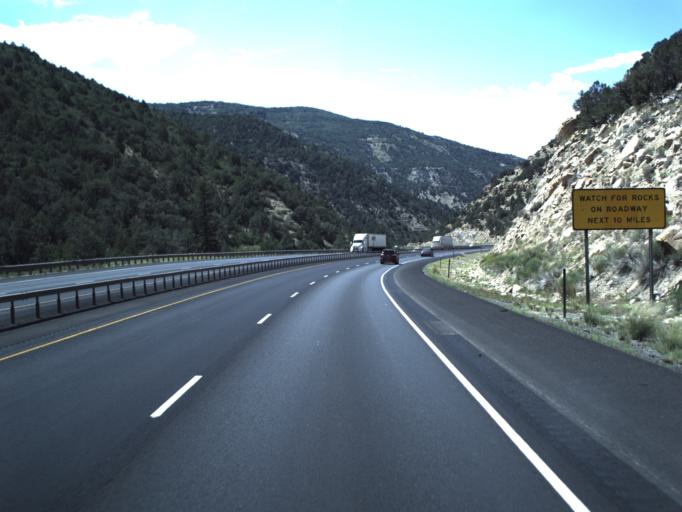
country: US
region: Utah
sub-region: Sevier County
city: Salina
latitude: 38.8819
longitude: -111.5814
